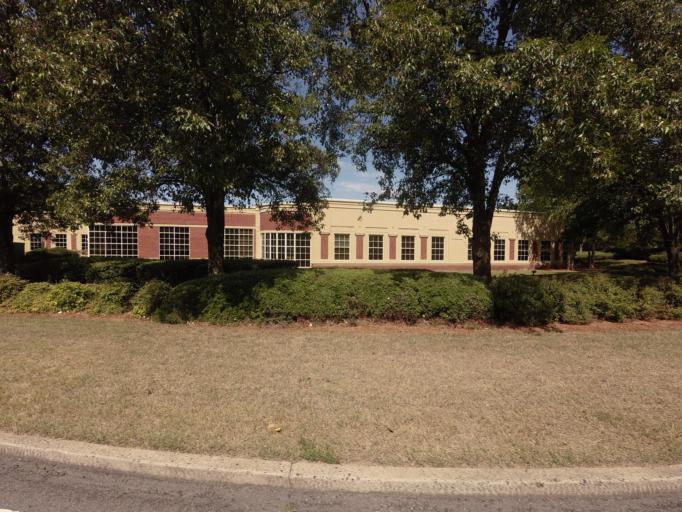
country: US
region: Georgia
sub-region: Fulton County
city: Johns Creek
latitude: 34.0629
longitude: -84.1650
